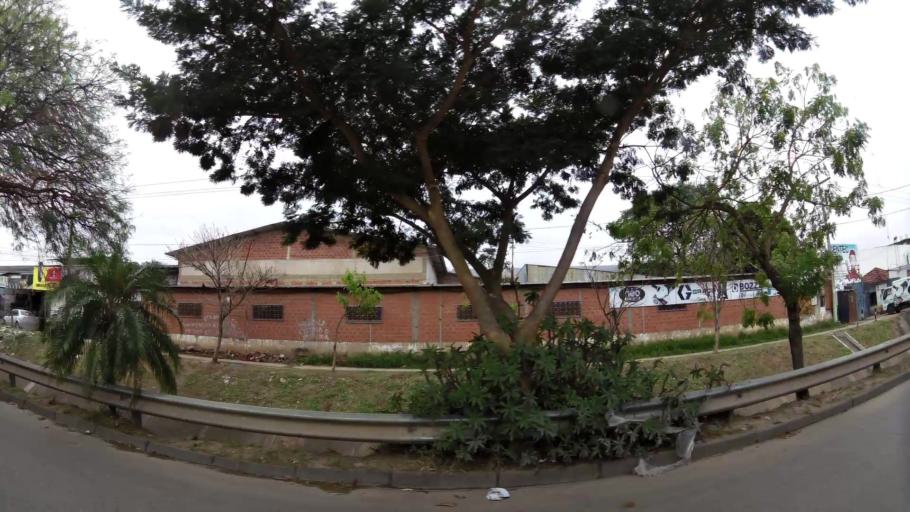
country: BO
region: Santa Cruz
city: Santa Cruz de la Sierra
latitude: -17.7902
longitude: -63.2069
